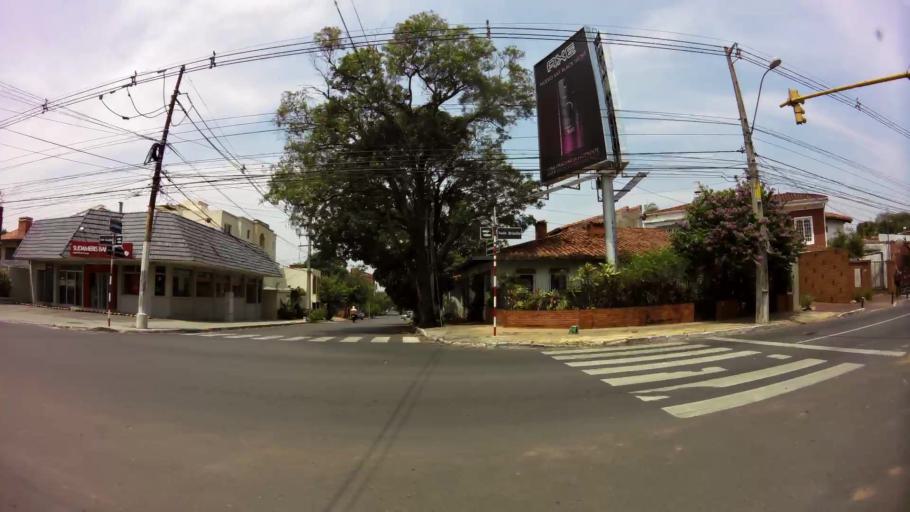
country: PY
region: Asuncion
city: Asuncion
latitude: -25.2834
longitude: -57.6011
